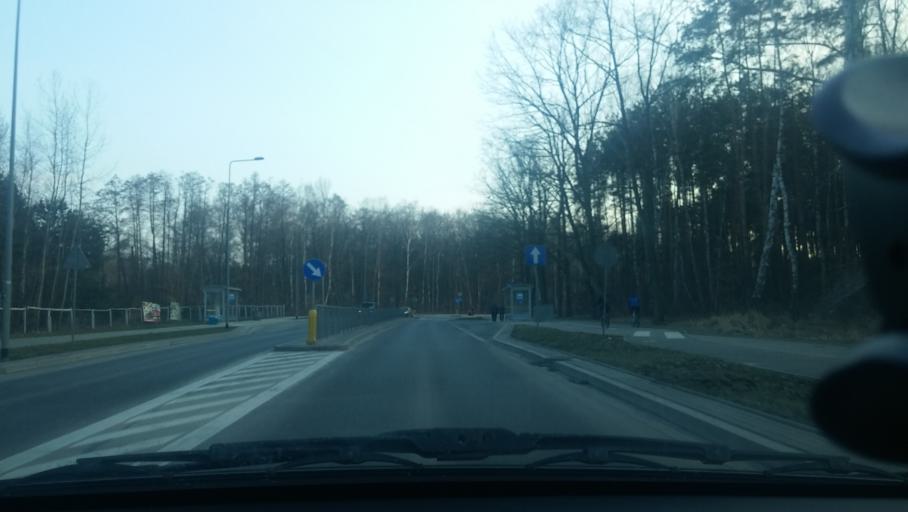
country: PL
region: Masovian Voivodeship
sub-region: Warszawa
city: Wesola
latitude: 52.2152
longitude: 21.2179
